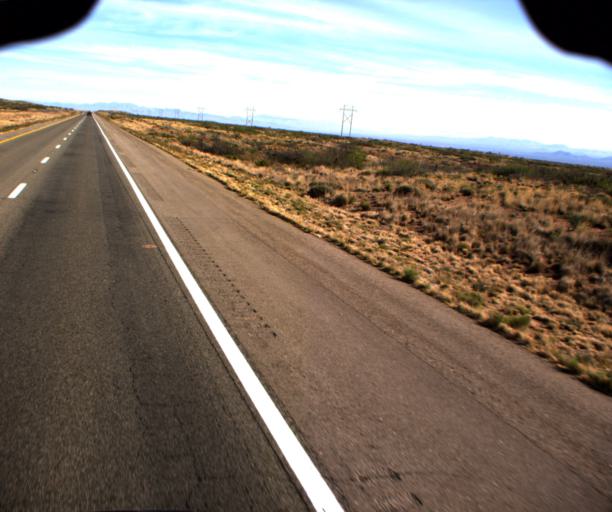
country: US
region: Arizona
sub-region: Graham County
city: Swift Trail Junction
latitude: 32.4895
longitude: -109.6732
